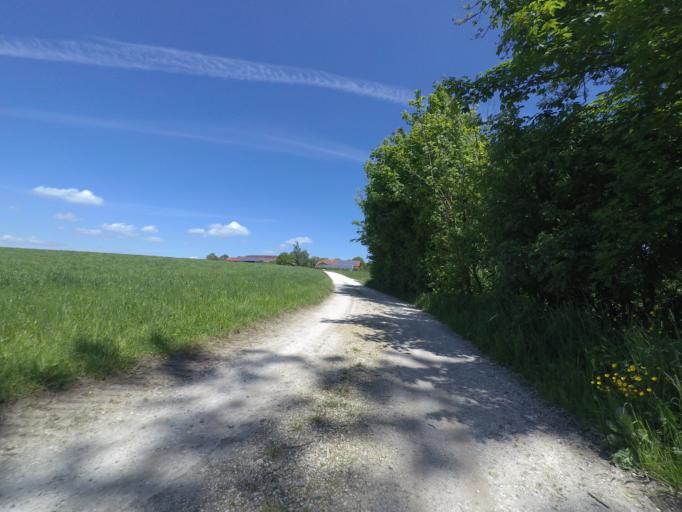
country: DE
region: Bavaria
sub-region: Upper Bavaria
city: Waging am See
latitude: 47.9499
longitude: 12.7752
